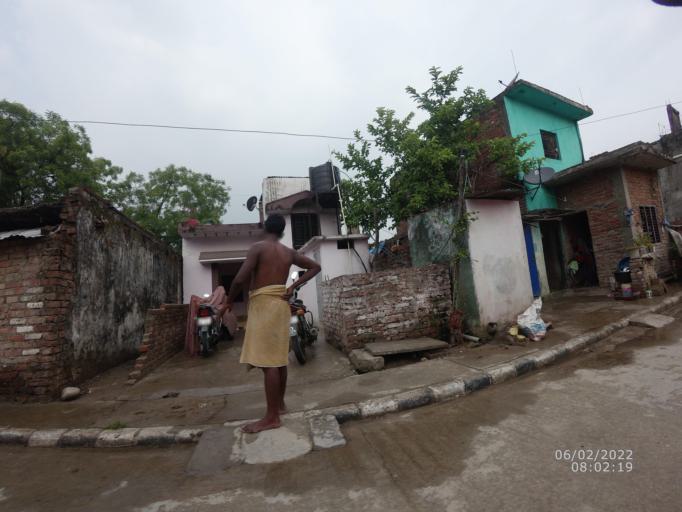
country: NP
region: Western Region
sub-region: Lumbini Zone
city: Bhairahawa
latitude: 27.4787
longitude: 83.4743
